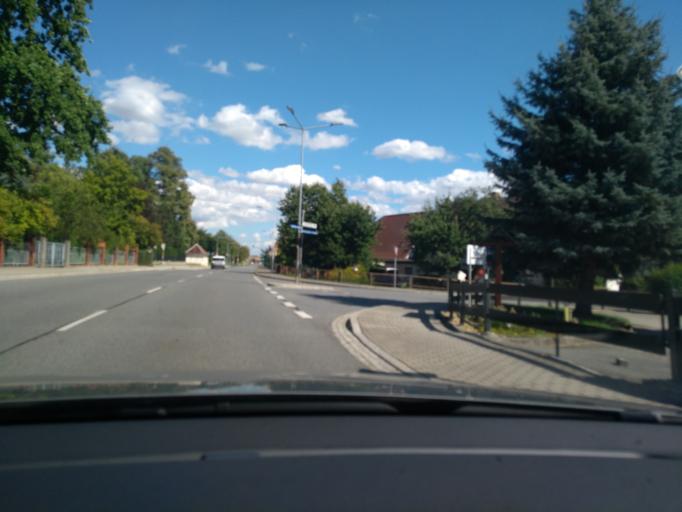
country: DE
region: Saxony
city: Goda
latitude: 51.1791
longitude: 14.3199
